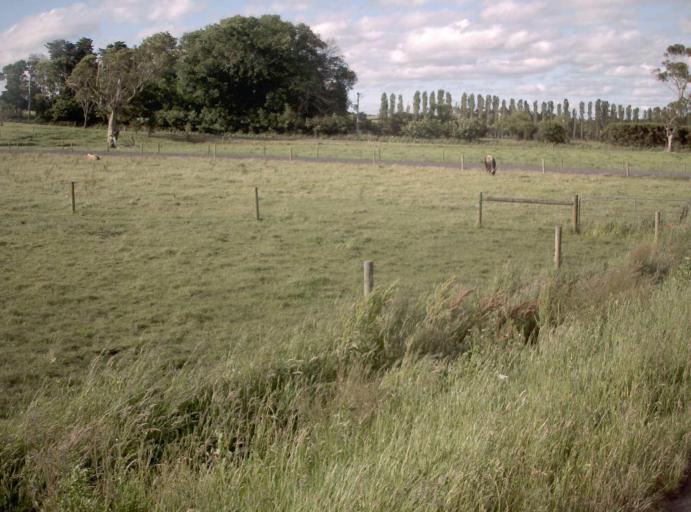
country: AU
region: Victoria
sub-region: Baw Baw
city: Warragul
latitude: -38.4926
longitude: 145.9283
